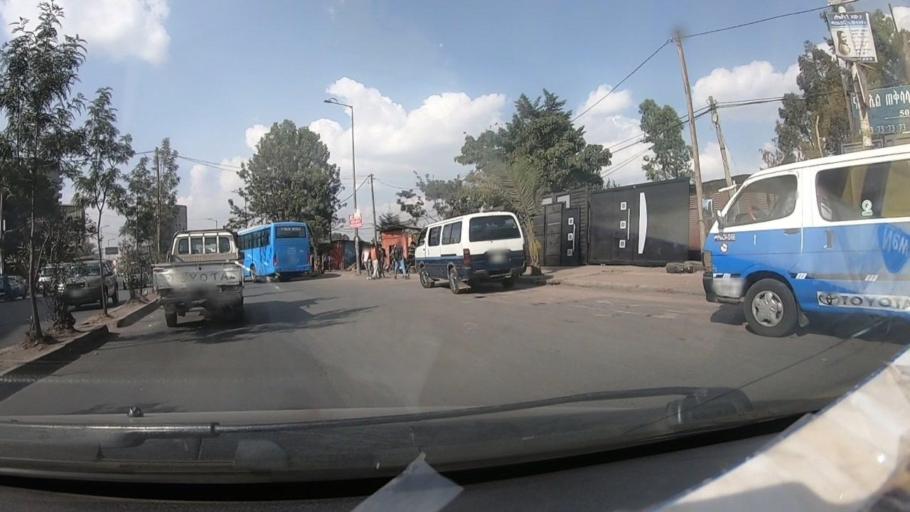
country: ET
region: Adis Abeba
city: Addis Ababa
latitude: 8.9650
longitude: 38.7334
